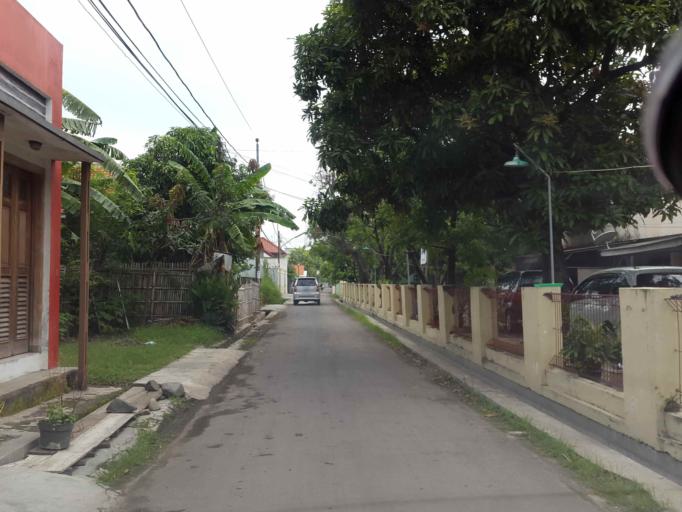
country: ID
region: Central Java
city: Dukuhturi
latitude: -6.8747
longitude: 109.0527
